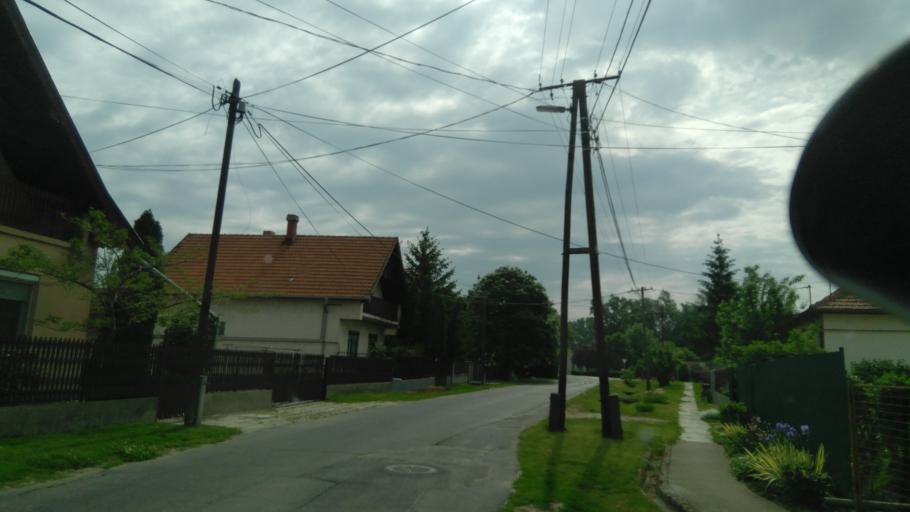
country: HU
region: Bekes
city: Szeghalom
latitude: 47.0139
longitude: 21.1700
